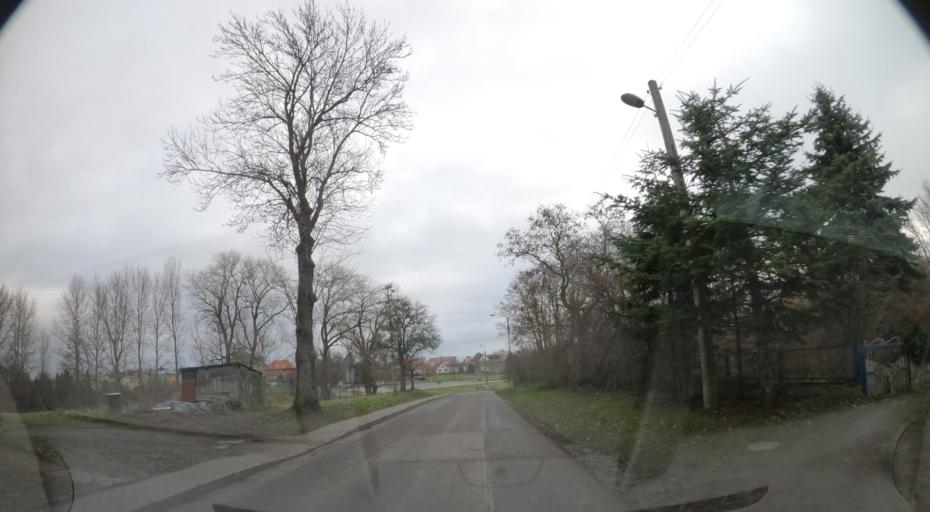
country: PL
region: Greater Poland Voivodeship
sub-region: Powiat pilski
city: Lobzenica
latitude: 53.2593
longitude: 17.2492
